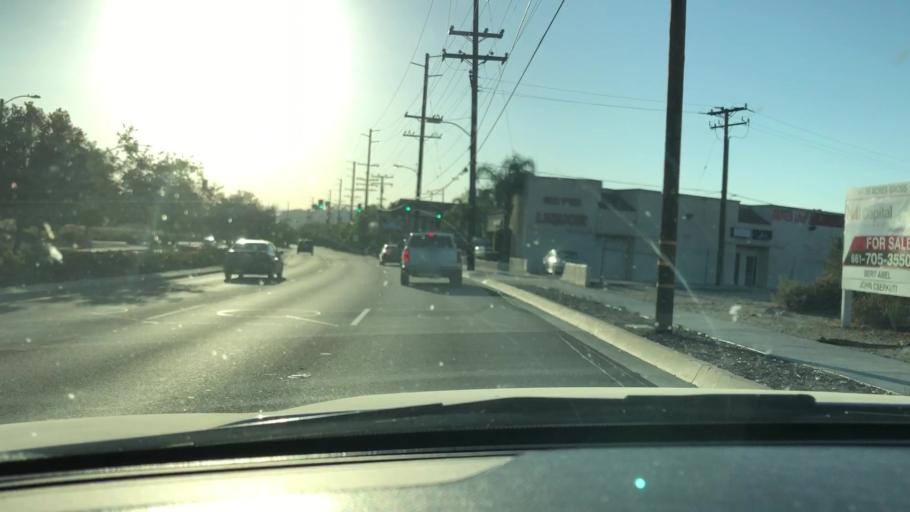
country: US
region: California
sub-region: Los Angeles County
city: Santa Clarita
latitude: 34.4204
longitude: -118.4837
